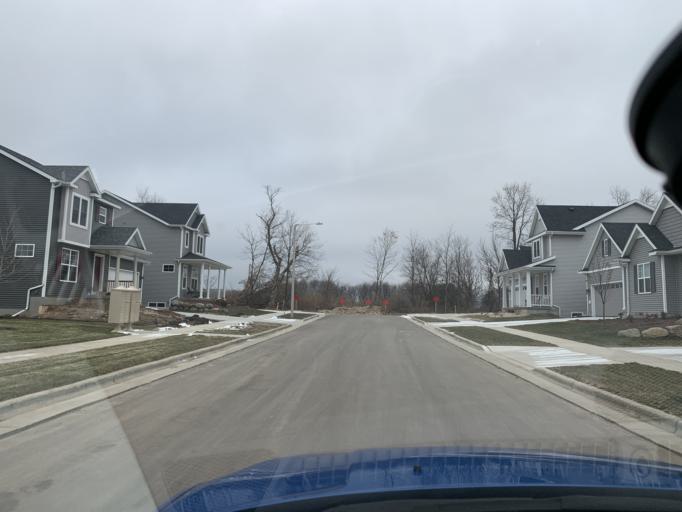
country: US
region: Wisconsin
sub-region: Dane County
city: Middleton
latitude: 43.0710
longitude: -89.5655
